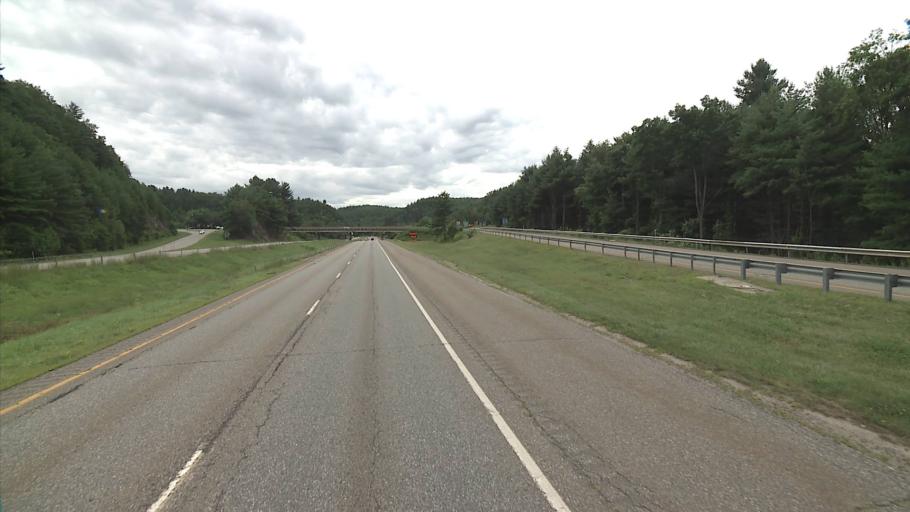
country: US
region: Connecticut
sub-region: Litchfield County
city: Torrington
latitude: 41.7650
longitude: -73.1154
